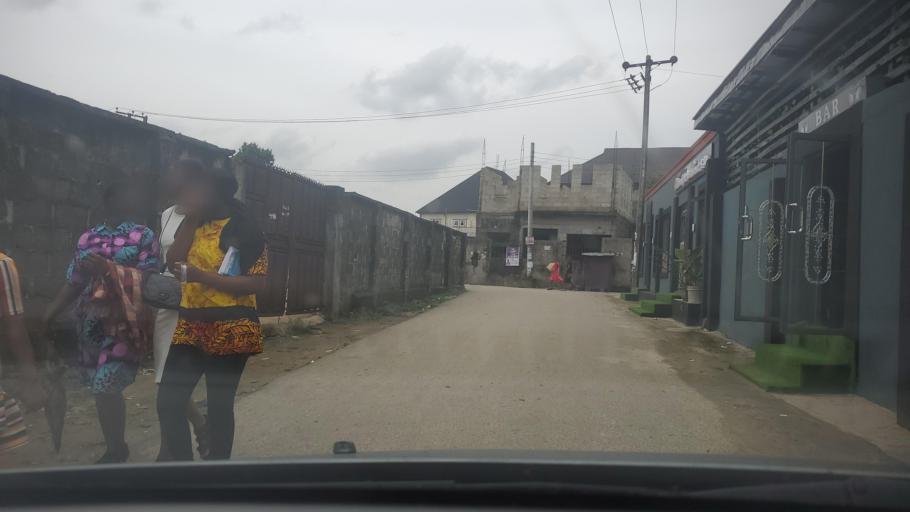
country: NG
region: Rivers
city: Port Harcourt
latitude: 4.8433
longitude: 6.9991
